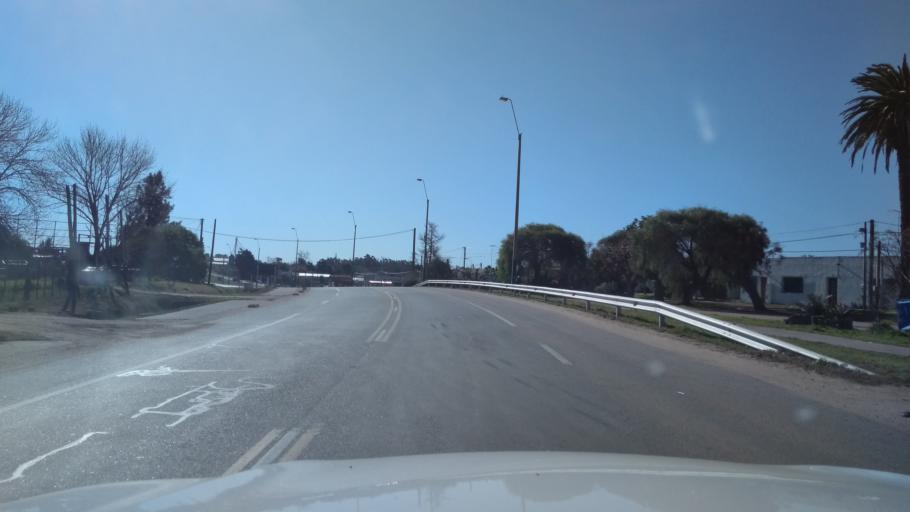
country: UY
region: Canelones
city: Atlantida
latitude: -34.7411
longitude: -55.7651
